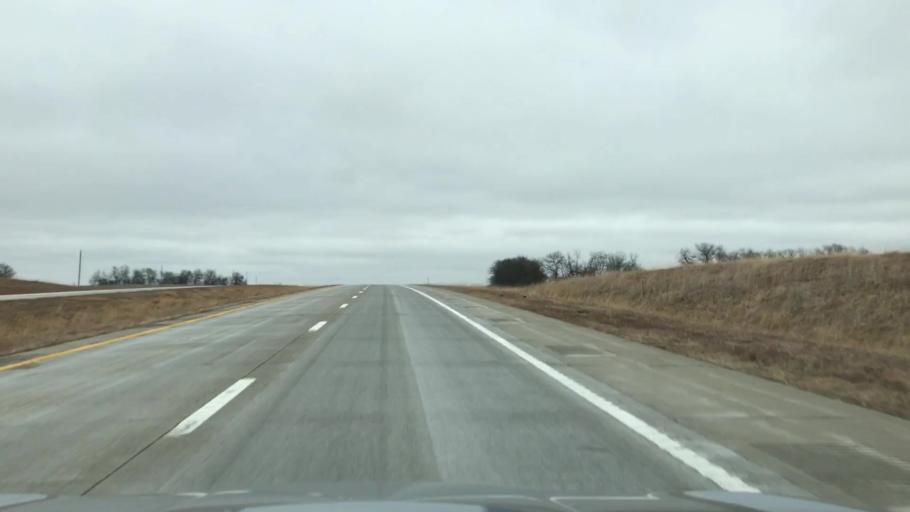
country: US
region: Missouri
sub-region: Livingston County
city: Chillicothe
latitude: 39.7348
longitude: -93.7677
